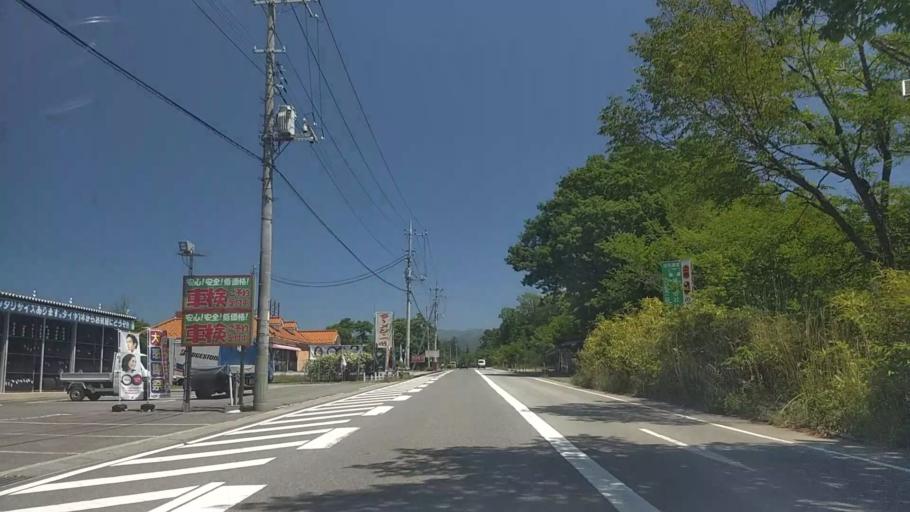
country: JP
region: Yamanashi
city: Nirasaki
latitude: 35.8092
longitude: 138.4284
